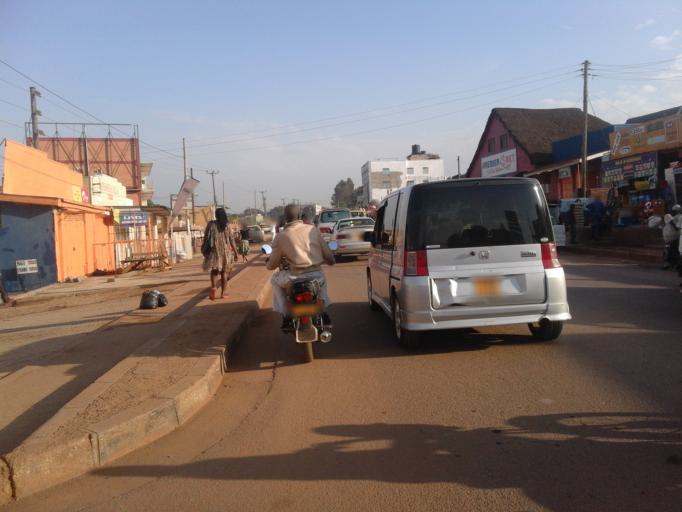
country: UG
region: Central Region
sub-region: Kampala District
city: Kampala
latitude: 0.2884
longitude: 32.6067
